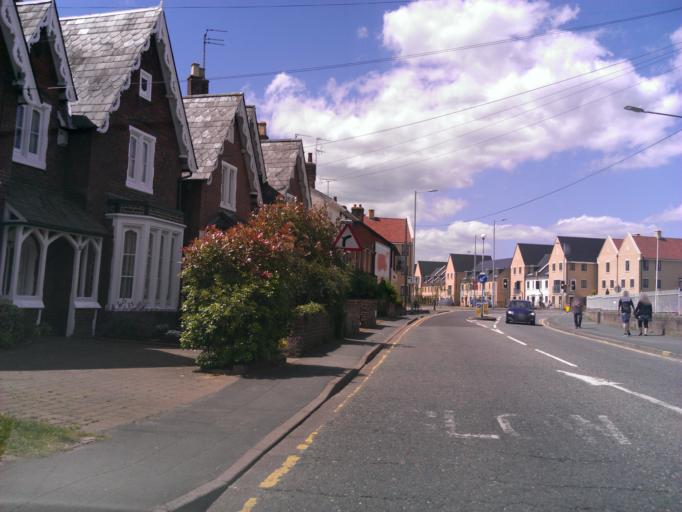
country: GB
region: England
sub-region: Essex
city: Colchester
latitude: 51.8816
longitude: 0.9111
